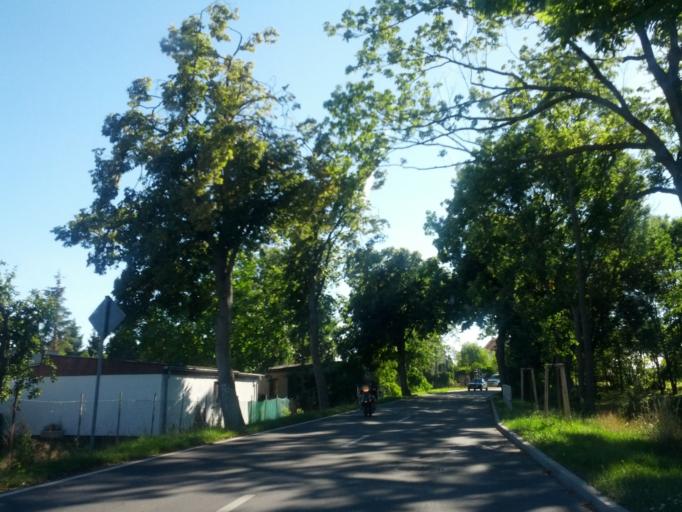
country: DE
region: Mecklenburg-Vorpommern
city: Bastorf
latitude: 54.1423
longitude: 11.7226
